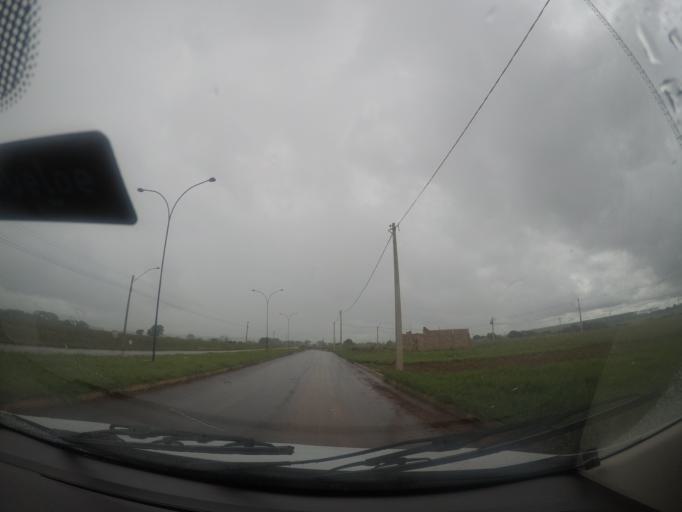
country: BR
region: Goias
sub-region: Trindade
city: Trindade
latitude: -16.6255
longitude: -49.4196
